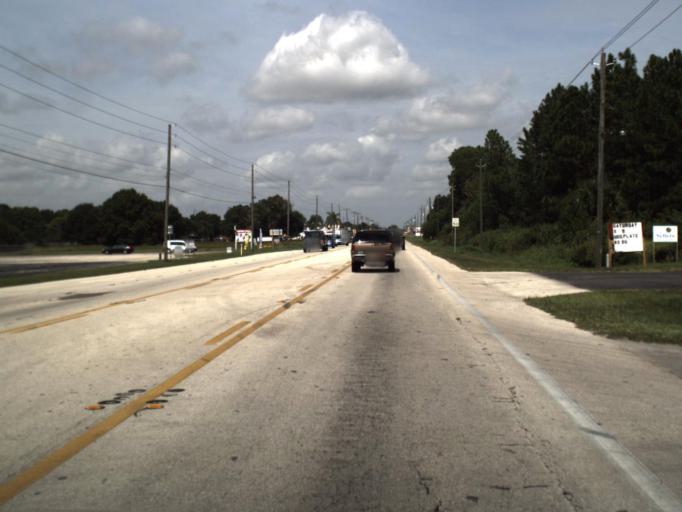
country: US
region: Florida
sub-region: Polk County
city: Jan-Phyl Village
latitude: 28.0174
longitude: -81.7607
